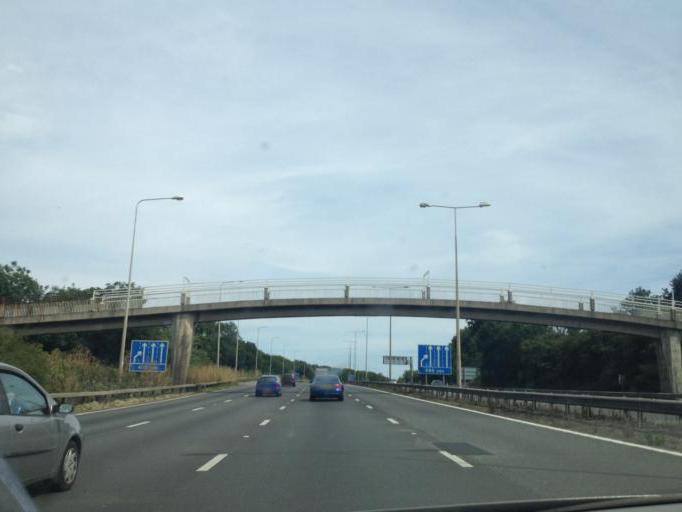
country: GB
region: England
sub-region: Hertfordshire
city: Bushey
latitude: 51.6466
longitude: -0.3343
